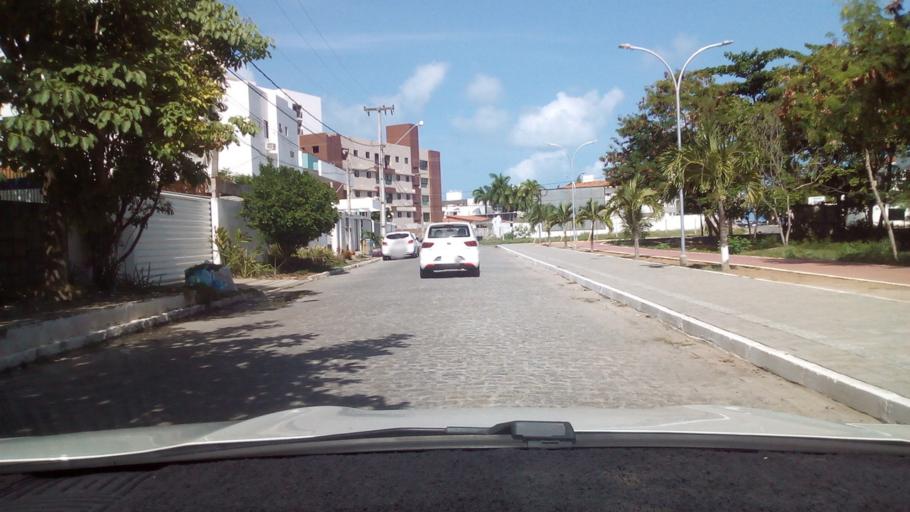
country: BR
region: Paraiba
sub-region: Joao Pessoa
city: Joao Pessoa
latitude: -7.0838
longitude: -34.8356
